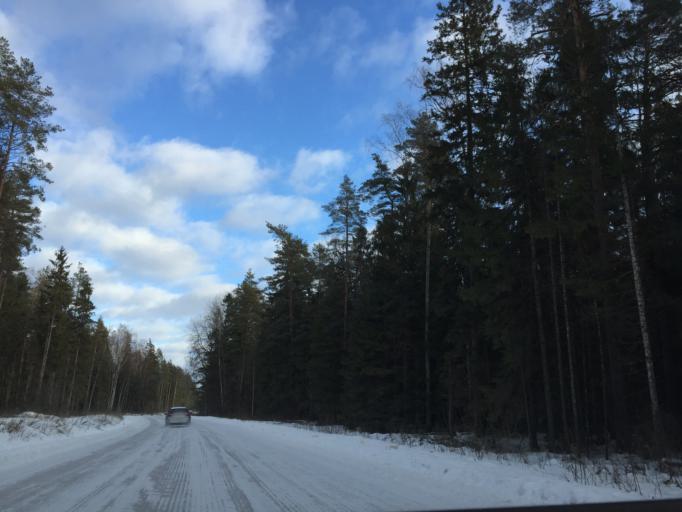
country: LV
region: Ogre
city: Jumprava
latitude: 56.5849
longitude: 24.9621
